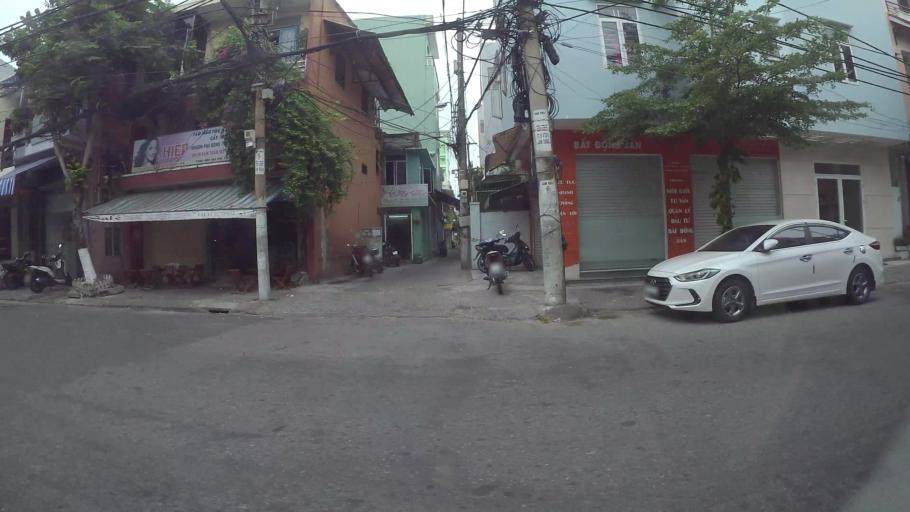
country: VN
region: Da Nang
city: Da Nang
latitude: 16.0780
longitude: 108.2146
